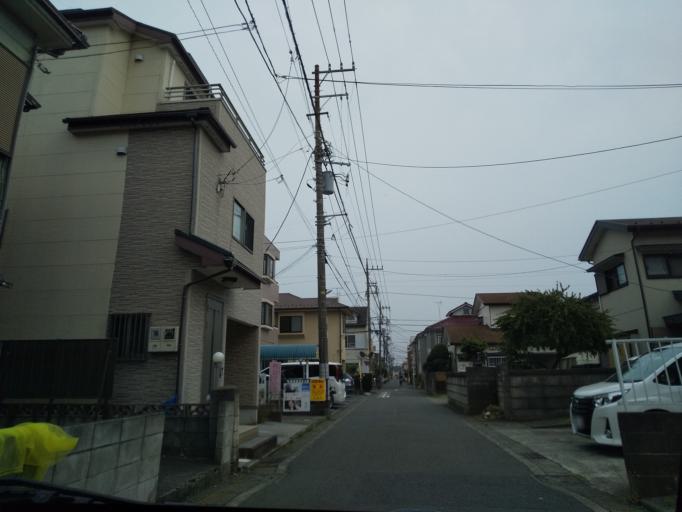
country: JP
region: Kanagawa
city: Minami-rinkan
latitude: 35.4663
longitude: 139.4257
